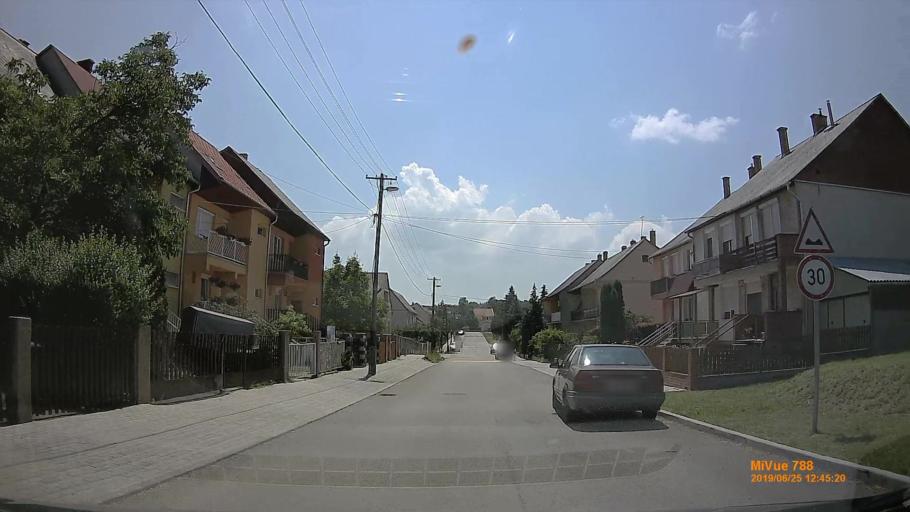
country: HU
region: Komarom-Esztergom
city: Esztergom
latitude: 47.8080
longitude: 18.7462
